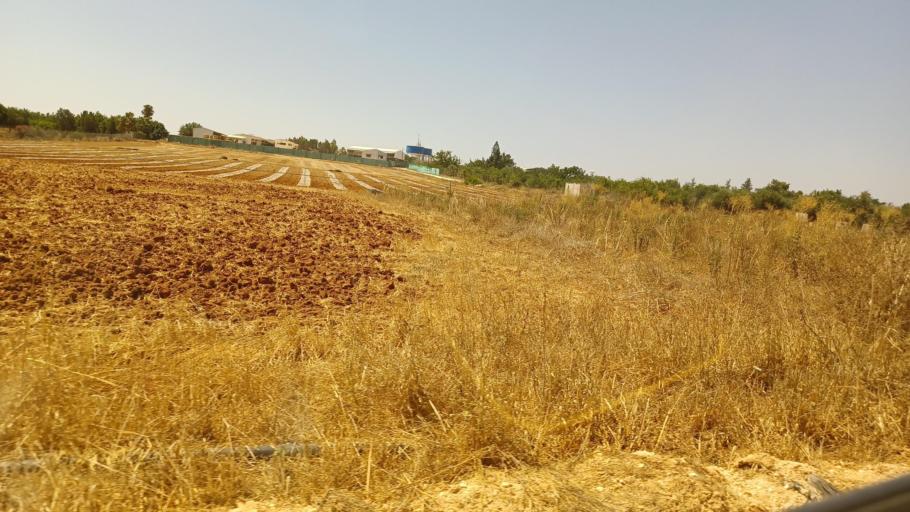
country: CY
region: Ammochostos
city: Acheritou
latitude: 35.0783
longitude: 33.8849
